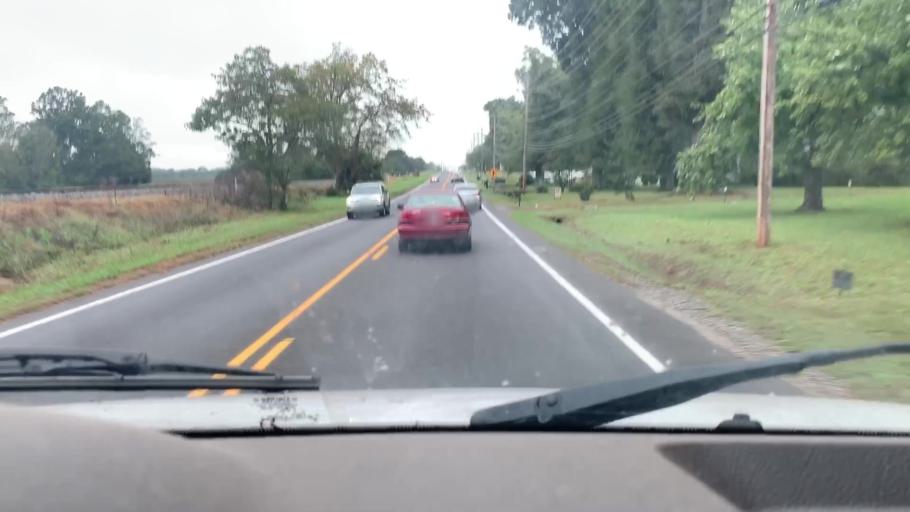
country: US
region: North Carolina
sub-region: Gaston County
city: Davidson
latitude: 35.5173
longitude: -80.8401
